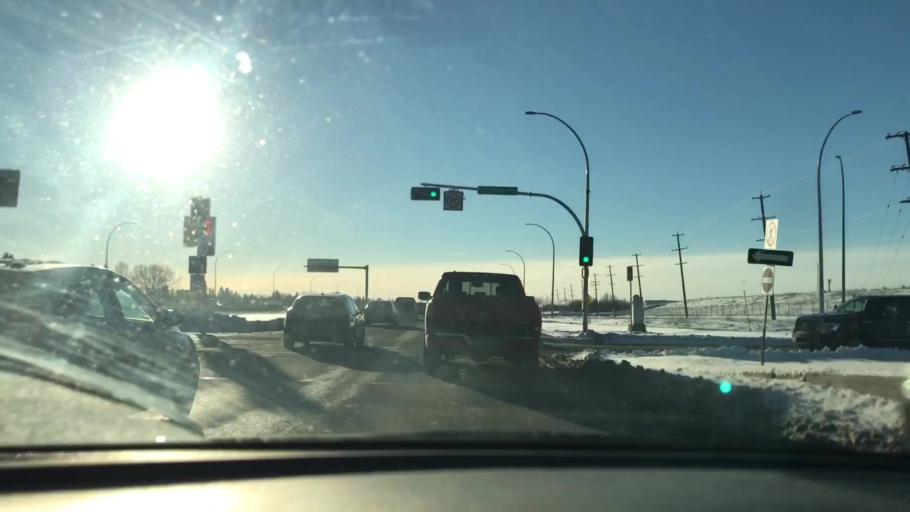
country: CA
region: Alberta
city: Edmonton
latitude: 53.4825
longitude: -113.4671
